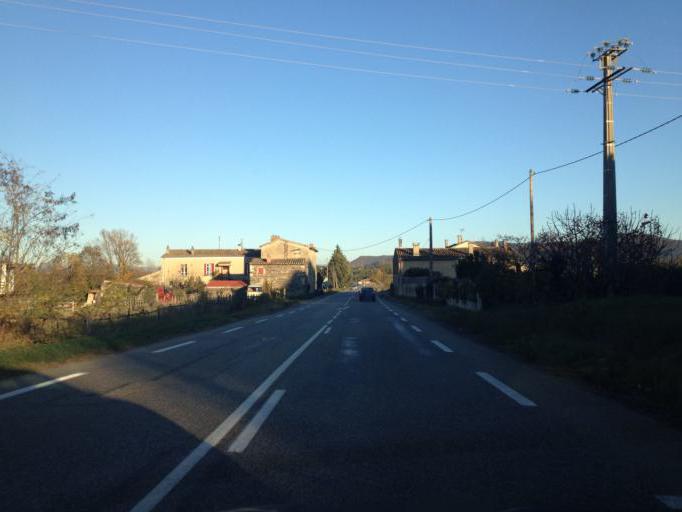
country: FR
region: Rhone-Alpes
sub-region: Departement de l'Ardeche
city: Chomerac
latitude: 44.7093
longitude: 4.6839
